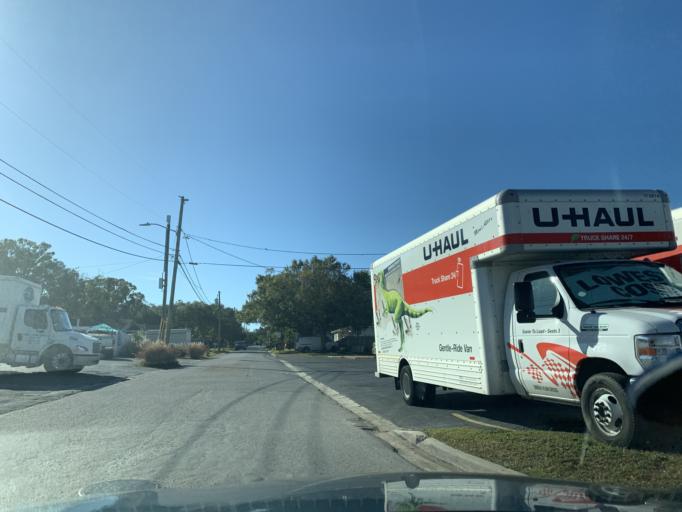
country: US
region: Florida
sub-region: Pinellas County
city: Lealman
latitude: 27.8283
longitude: -82.6767
